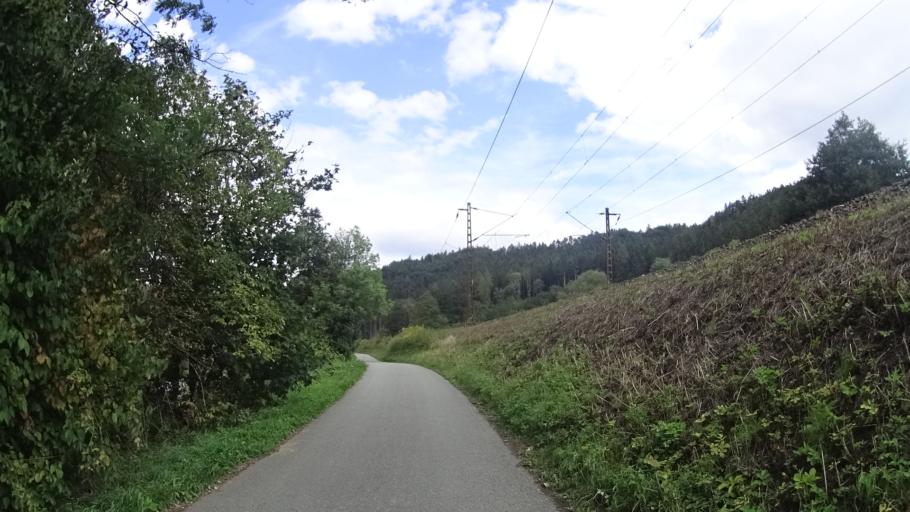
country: CZ
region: Pardubicky
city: Brandys nad Orlici
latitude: 49.9813
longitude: 16.3360
